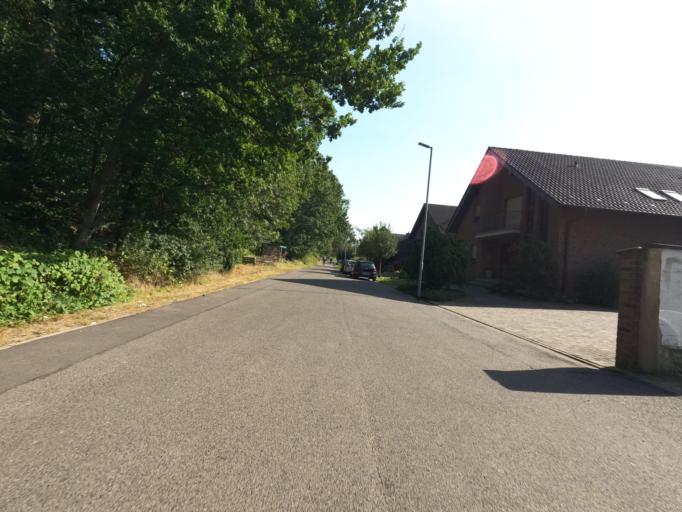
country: DE
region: North Rhine-Westphalia
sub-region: Regierungsbezirk Koln
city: Linnich
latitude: 50.9598
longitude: 6.2641
